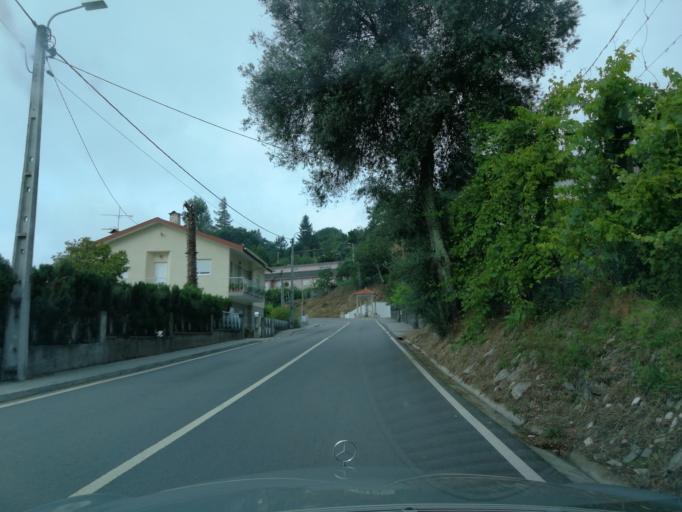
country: PT
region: Braga
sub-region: Braga
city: Braga
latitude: 41.5199
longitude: -8.3685
